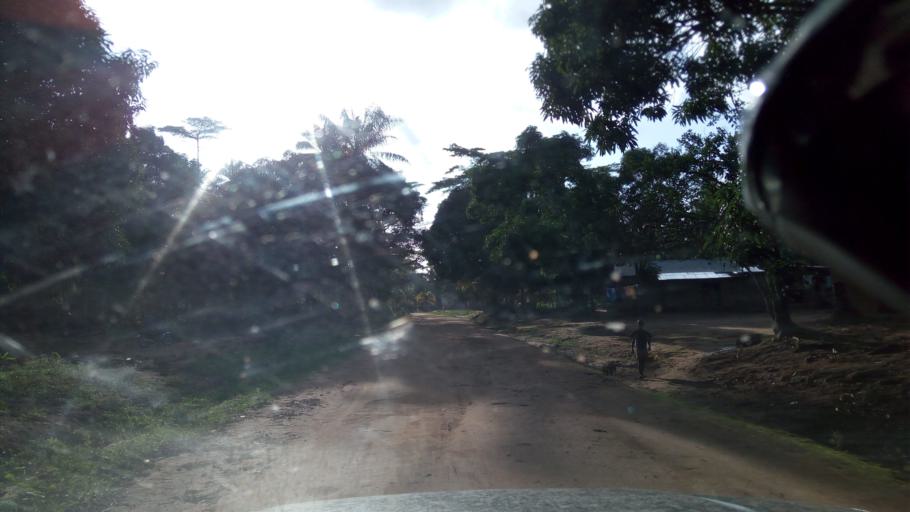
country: SL
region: Northern Province
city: Sawkta
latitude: 8.6989
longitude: -13.1099
